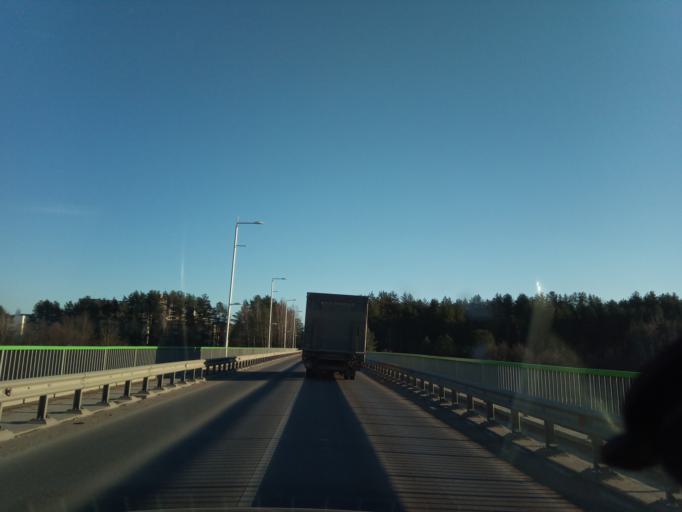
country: LT
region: Alytaus apskritis
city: Druskininkai
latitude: 54.0270
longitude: 23.9942
